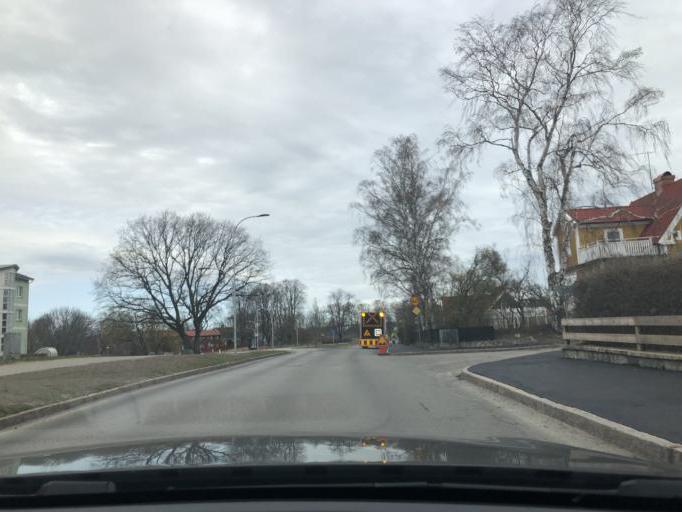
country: SE
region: Kalmar
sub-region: Kalmar Kommun
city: Kalmar
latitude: 56.6670
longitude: 16.3206
